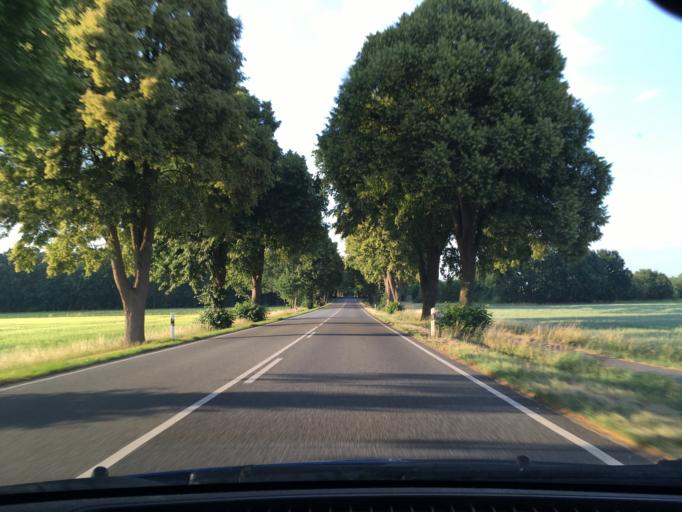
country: DE
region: Lower Saxony
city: Celle
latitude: 52.6662
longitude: 10.1356
